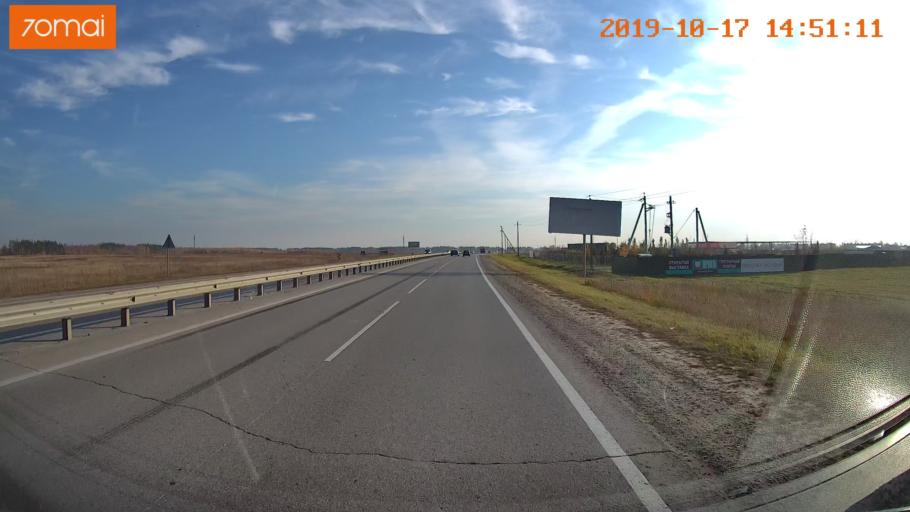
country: RU
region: Rjazan
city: Polyany
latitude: 54.7234
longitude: 39.8468
